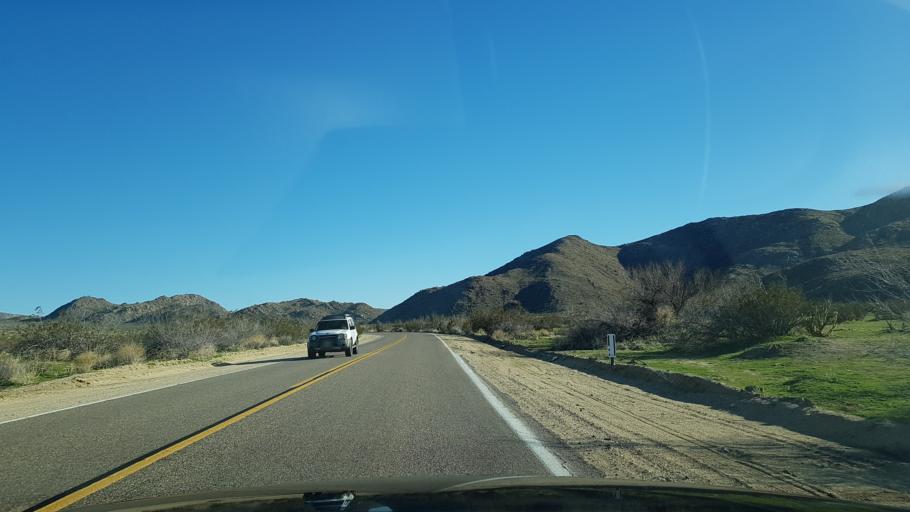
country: US
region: California
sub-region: San Diego County
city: Julian
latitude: 33.0532
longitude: -116.4187
